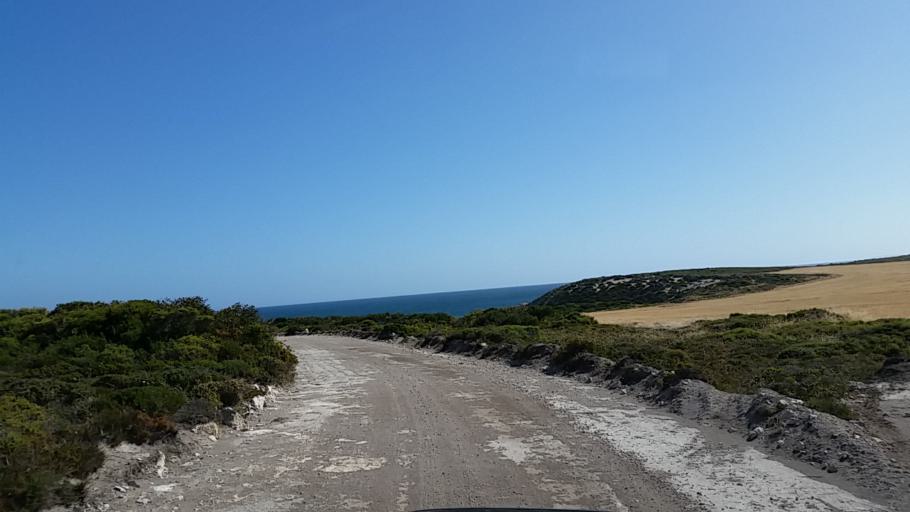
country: AU
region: South Australia
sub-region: Yorke Peninsula
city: Honiton
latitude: -35.2382
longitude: 137.1482
